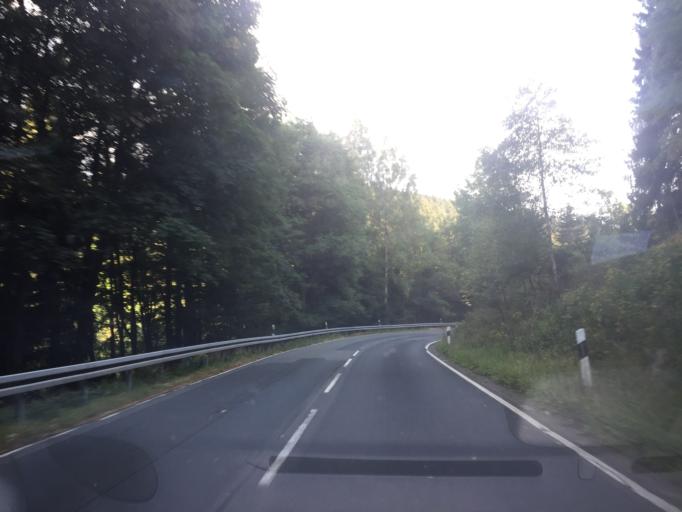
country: DE
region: Lower Saxony
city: Wieda
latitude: 51.6711
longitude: 10.5932
